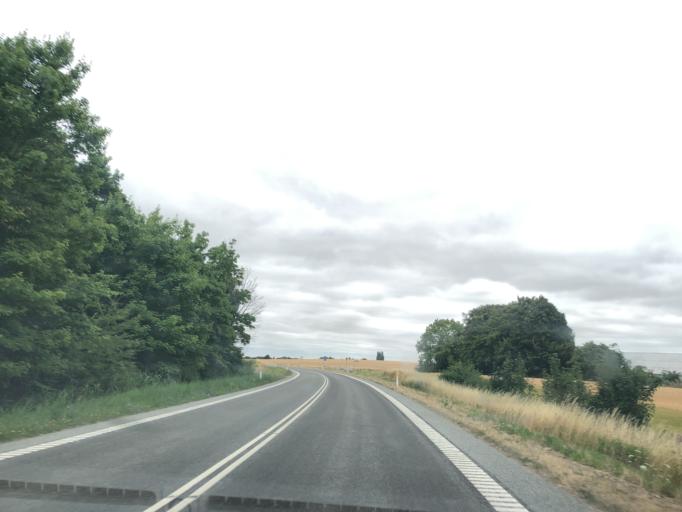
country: DK
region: Zealand
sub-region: Slagelse Kommune
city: Skaelskor
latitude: 55.2179
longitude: 11.2993
